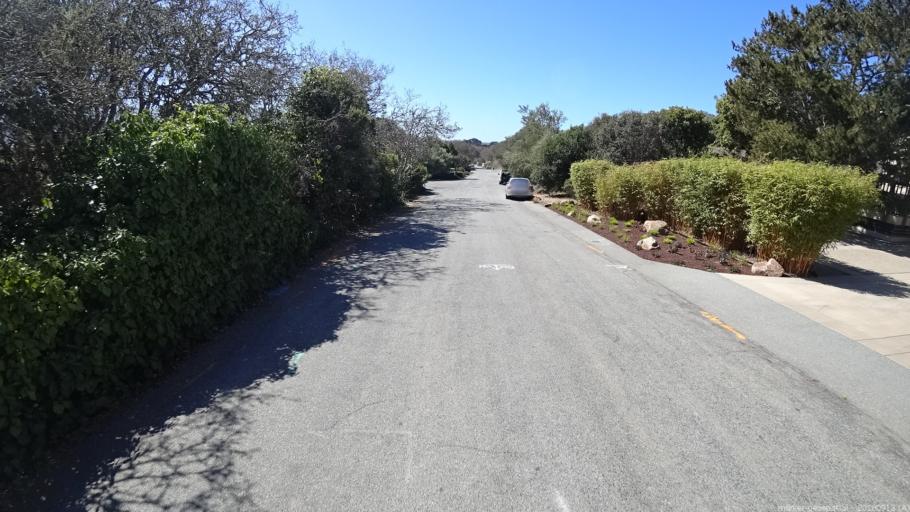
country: US
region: California
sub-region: Monterey County
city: Carmel-by-the-Sea
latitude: 36.5447
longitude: -121.9262
